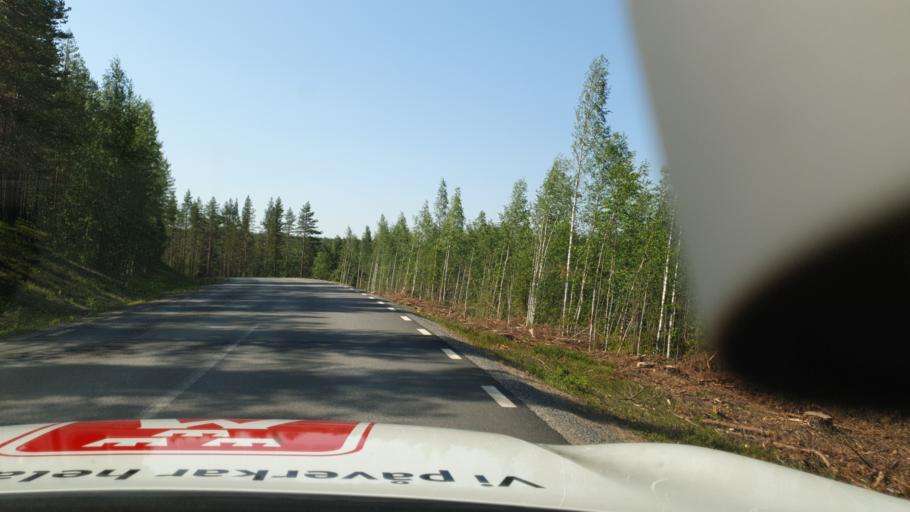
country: SE
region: Vaesterbotten
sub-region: Skelleftea Kommun
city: Langsele
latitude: 64.9506
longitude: 20.0254
